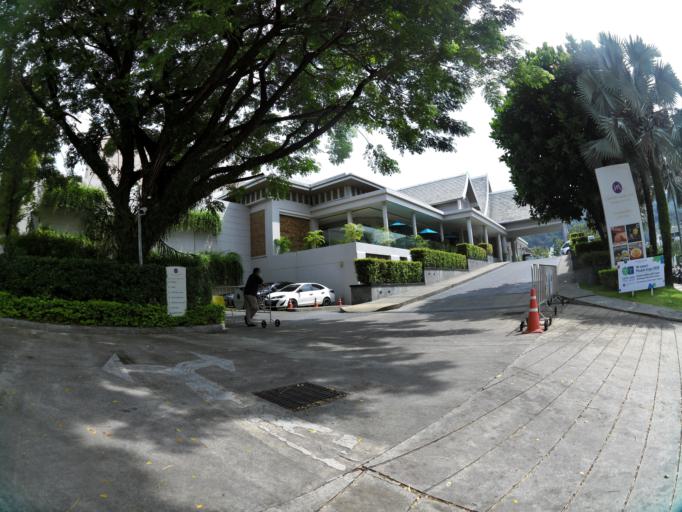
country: TH
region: Phuket
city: Patong
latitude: 7.8879
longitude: 98.2960
